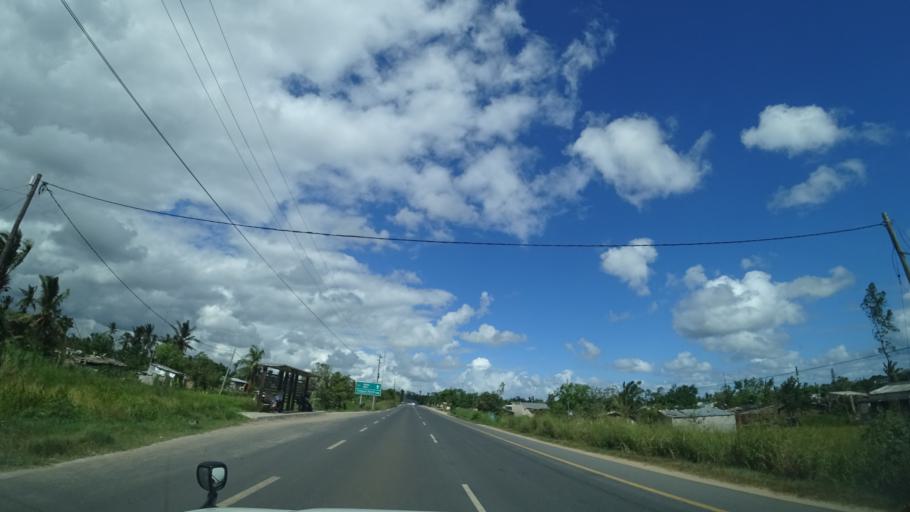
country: MZ
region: Sofala
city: Dondo
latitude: -19.5281
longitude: 34.6269
